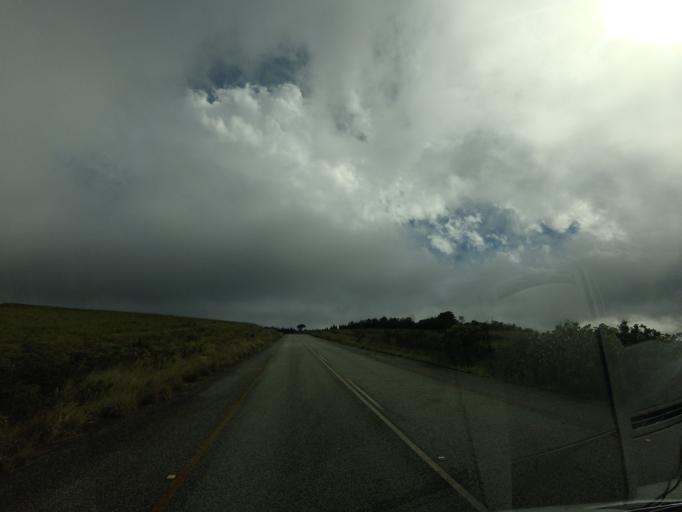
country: ZA
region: Mpumalanga
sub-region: Ehlanzeni District
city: Graksop
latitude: -24.8576
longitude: 30.8904
